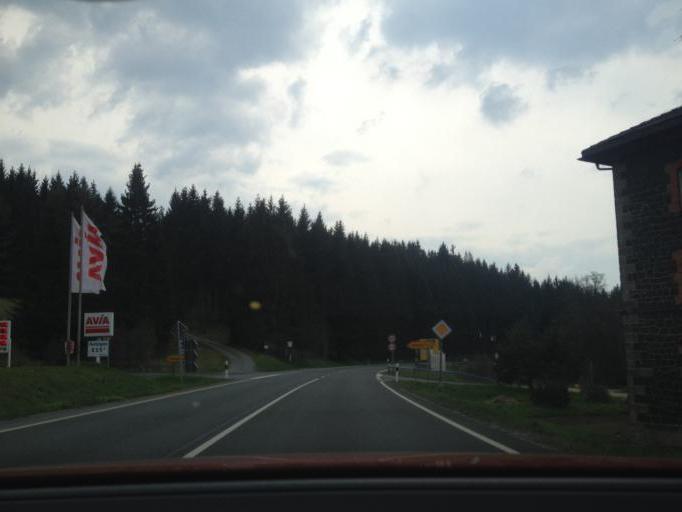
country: DE
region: Bavaria
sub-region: Upper Franconia
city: Bischofsgrun
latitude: 50.0560
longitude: 11.7816
